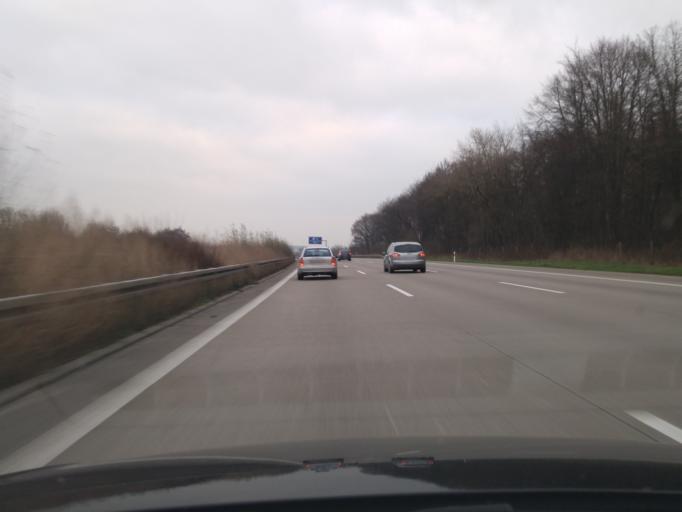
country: DE
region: Saxony-Anhalt
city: Beendorf
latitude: 52.2085
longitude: 11.1149
